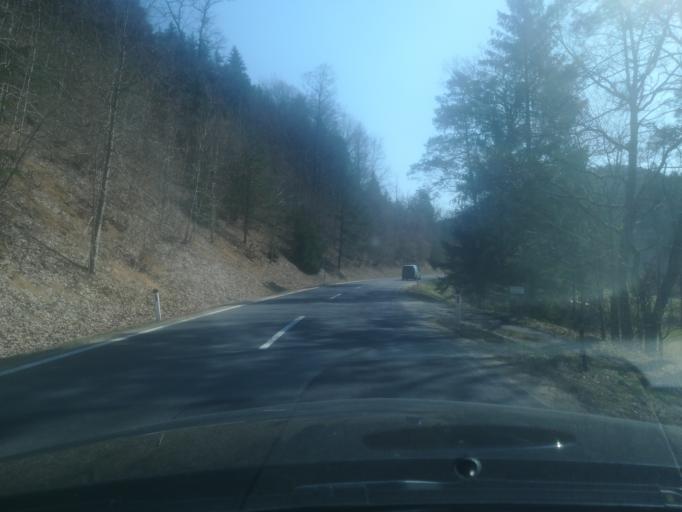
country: AT
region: Upper Austria
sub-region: Politischer Bezirk Freistadt
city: Freistadt
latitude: 48.4431
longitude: 14.5513
